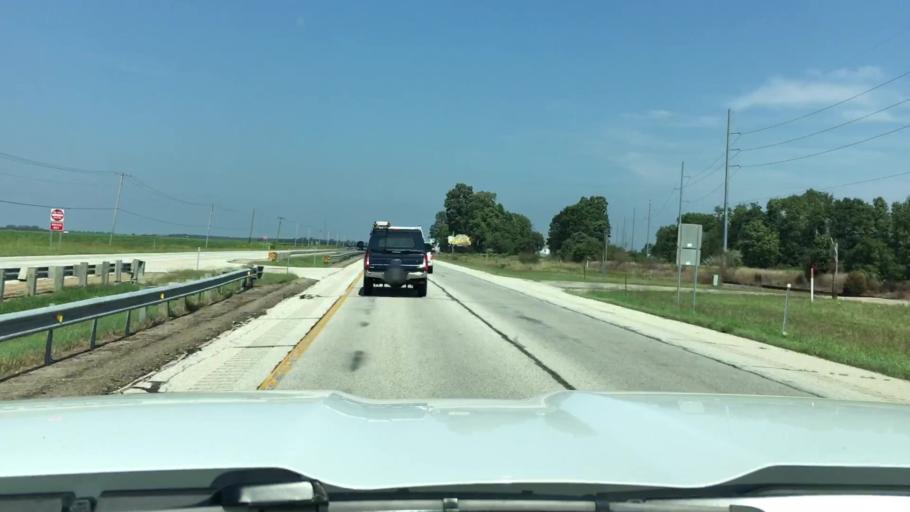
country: US
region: Michigan
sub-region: Kalamazoo County
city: Schoolcraft
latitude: 42.0673
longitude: -85.6363
